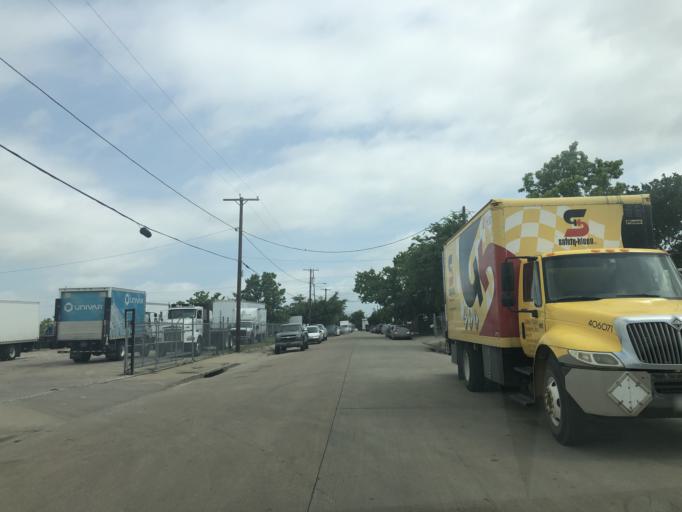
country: US
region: Texas
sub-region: Dallas County
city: Cockrell Hill
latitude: 32.8042
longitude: -96.8763
